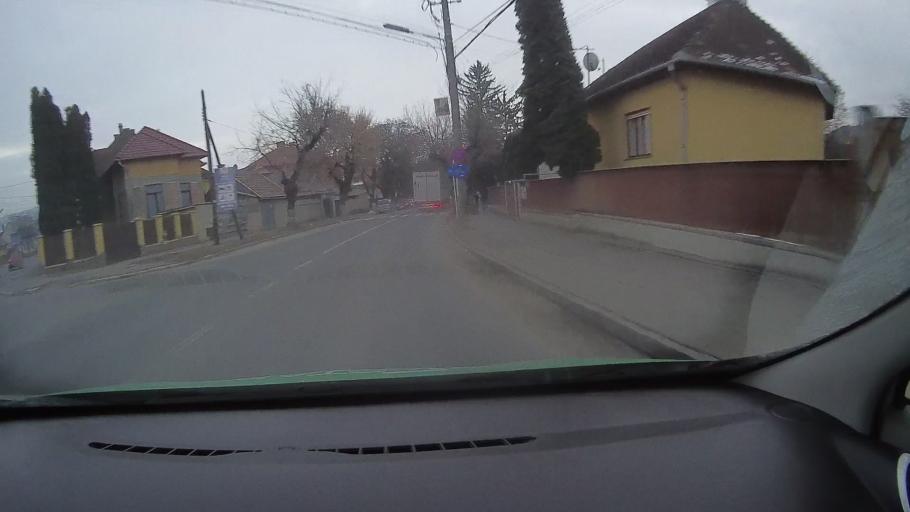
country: RO
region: Harghita
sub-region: Municipiul Odorheiu Secuiesc
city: Odorheiu Secuiesc
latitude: 46.3142
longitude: 25.2864
